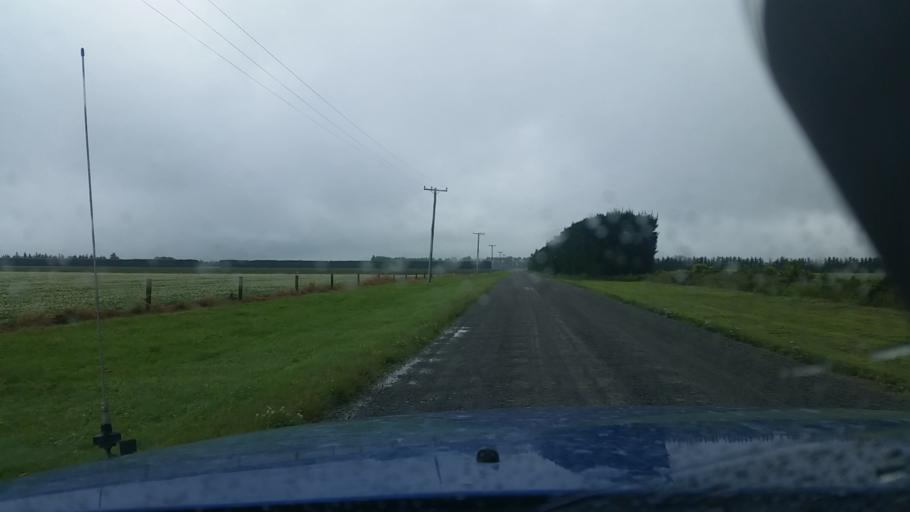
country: NZ
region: Canterbury
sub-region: Ashburton District
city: Methven
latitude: -43.6582
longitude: 171.8102
